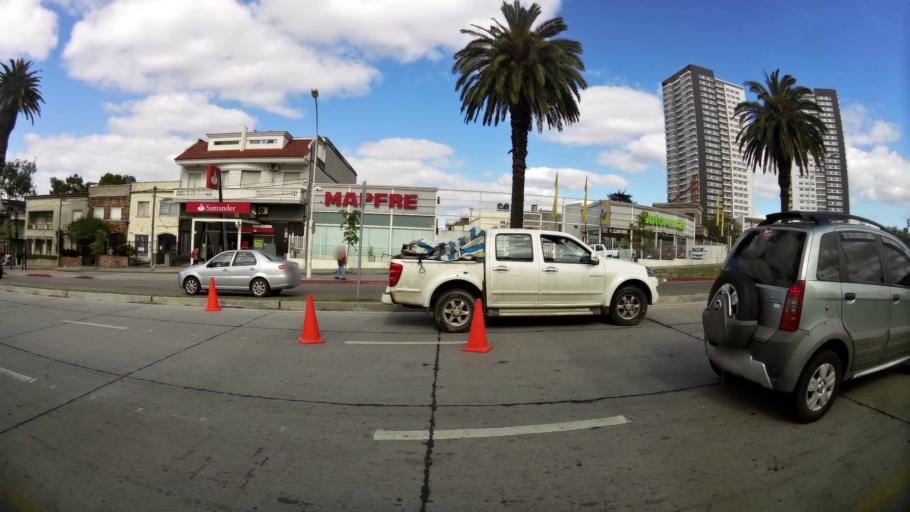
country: UY
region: Montevideo
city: Montevideo
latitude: -34.8703
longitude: -56.1675
